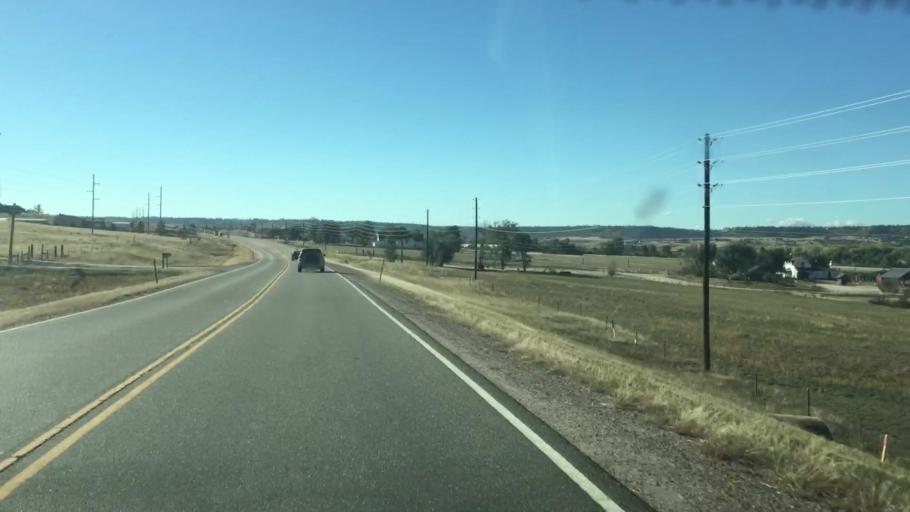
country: US
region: Colorado
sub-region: Douglas County
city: The Pinery
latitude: 39.4117
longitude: -104.7608
